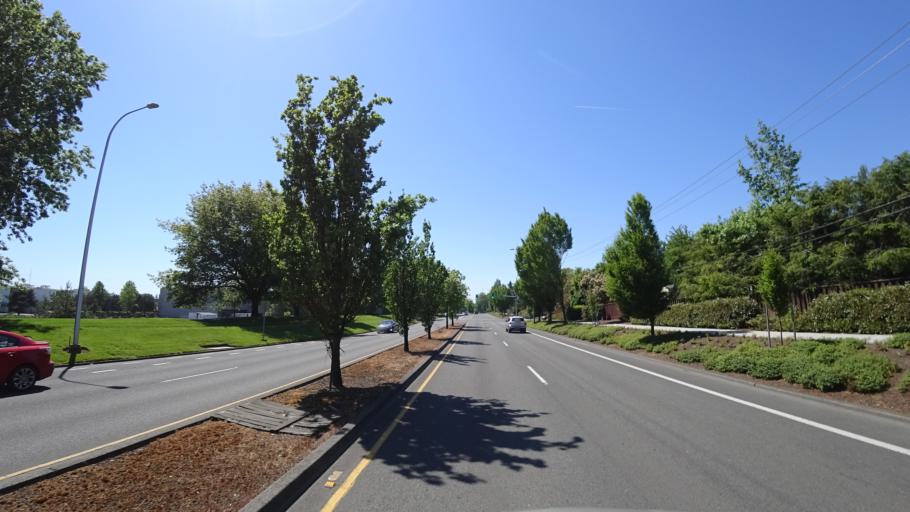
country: US
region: Oregon
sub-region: Washington County
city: Rockcreek
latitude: 45.5337
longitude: -122.9249
